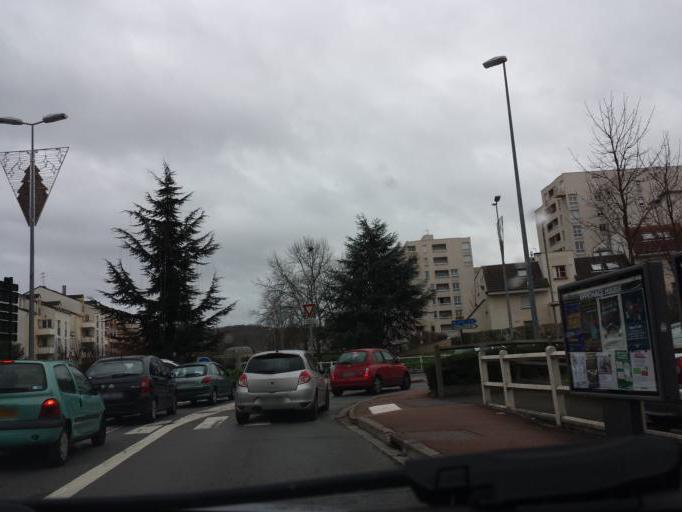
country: FR
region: Ile-de-France
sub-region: Departement du Val-d'Oise
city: Franconville
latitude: 48.9825
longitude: 2.2462
